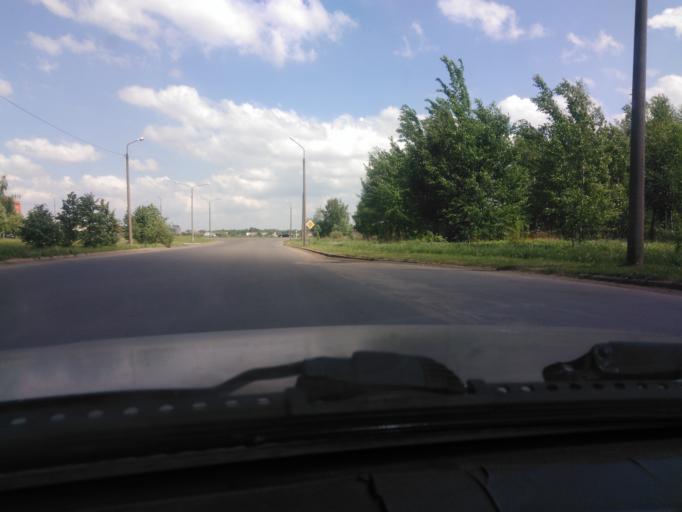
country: BY
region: Mogilev
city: Palykavichy Pyershyya
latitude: 53.9480
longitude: 30.3740
